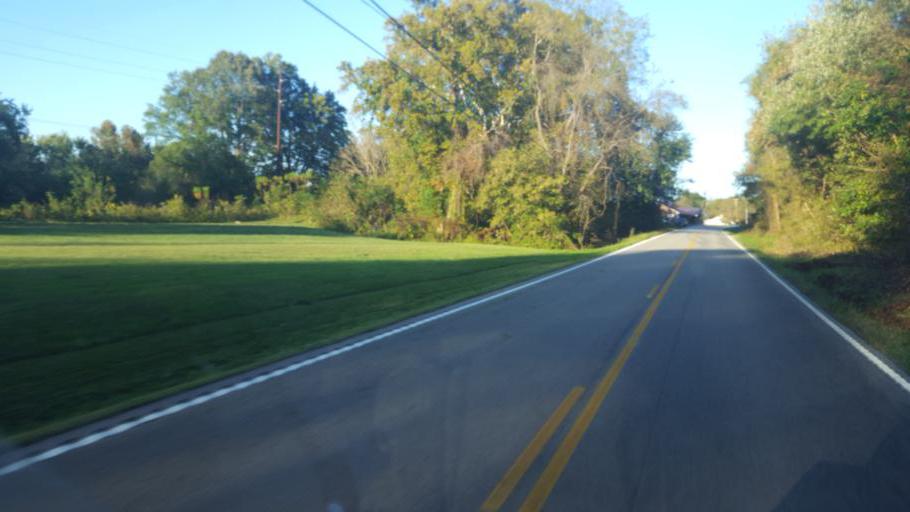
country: US
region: Ohio
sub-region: Scioto County
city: Portsmouth
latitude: 38.6845
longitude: -83.0636
